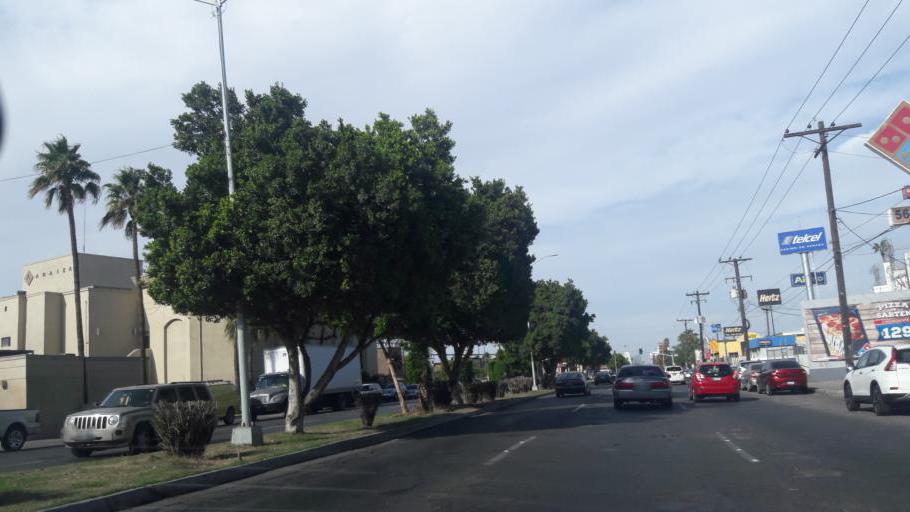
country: MX
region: Baja California
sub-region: Mexicali
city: Mexicali
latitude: 32.6425
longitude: -115.4504
